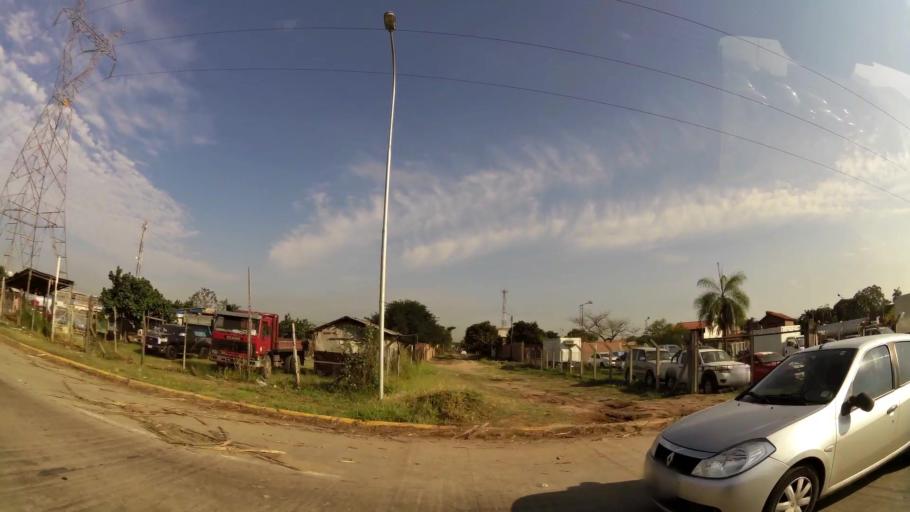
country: BO
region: Santa Cruz
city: Santa Cruz de la Sierra
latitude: -17.7269
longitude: -63.1355
